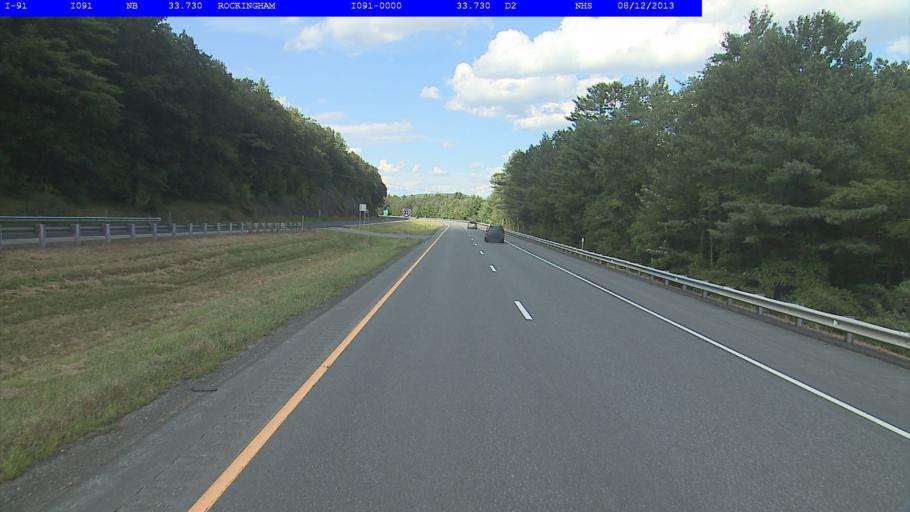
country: US
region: Vermont
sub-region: Windham County
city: Bellows Falls
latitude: 43.1587
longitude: -72.4681
